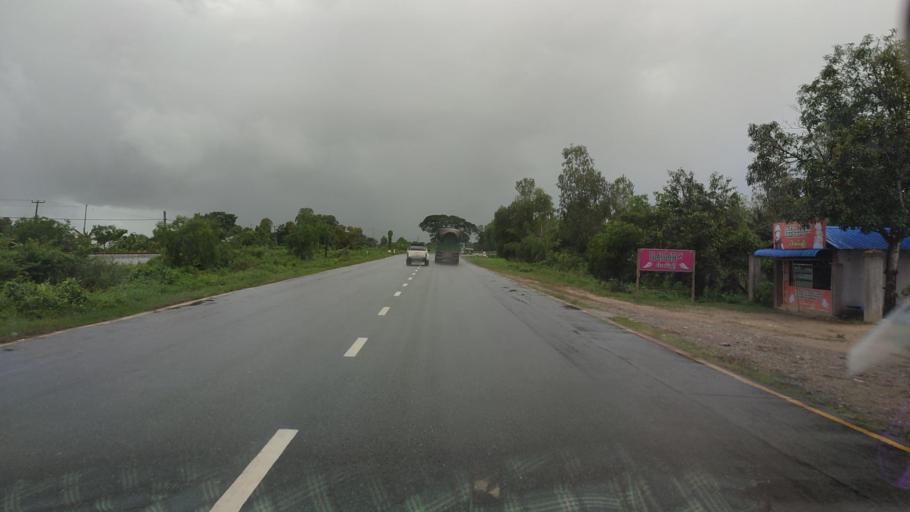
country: MM
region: Bago
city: Bago
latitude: 17.6180
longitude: 96.5728
